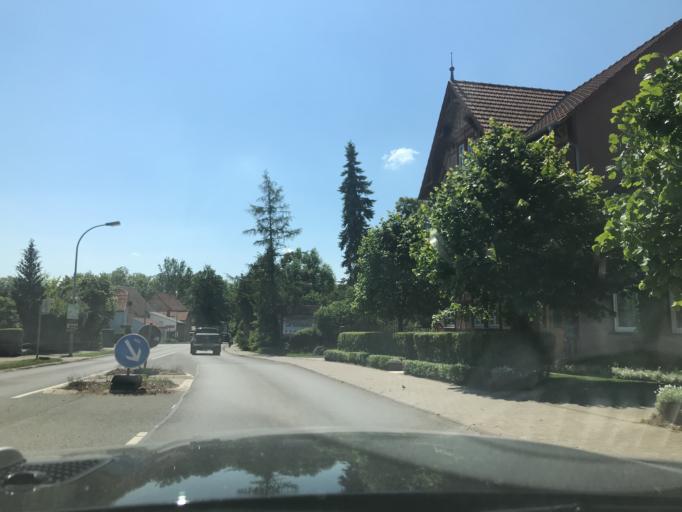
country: DE
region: Thuringia
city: Westhausen
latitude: 51.0148
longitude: 10.6841
